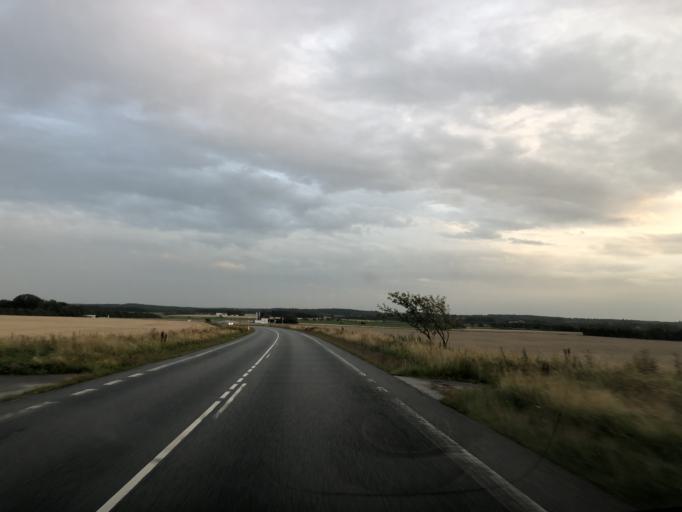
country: DK
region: Central Jutland
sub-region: Holstebro Kommune
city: Vinderup
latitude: 56.5753
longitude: 8.8709
